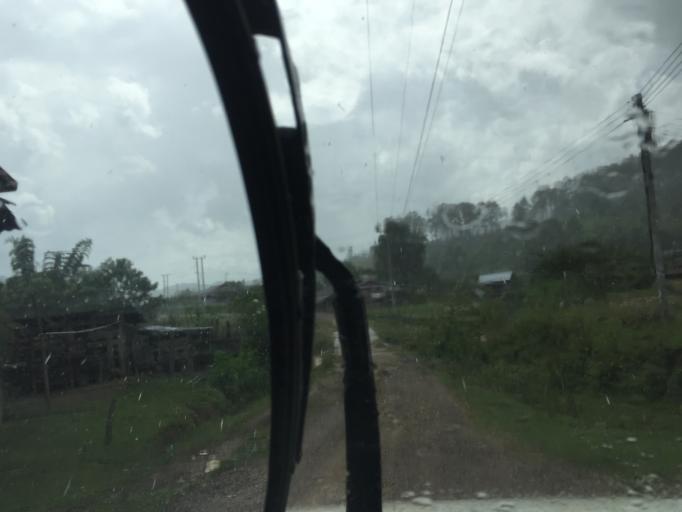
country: LA
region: Xiangkhoang
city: Muang Phonsavan
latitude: 19.3396
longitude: 103.5799
